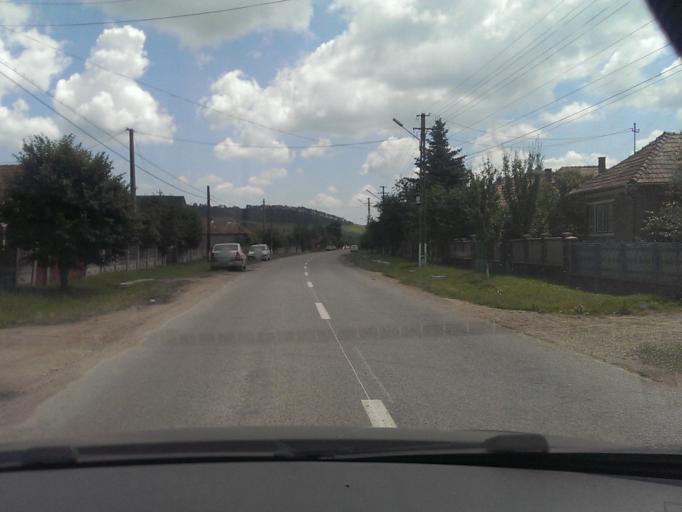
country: RO
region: Cluj
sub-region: Comuna Bontida
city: Rascruci
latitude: 46.9250
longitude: 23.7973
